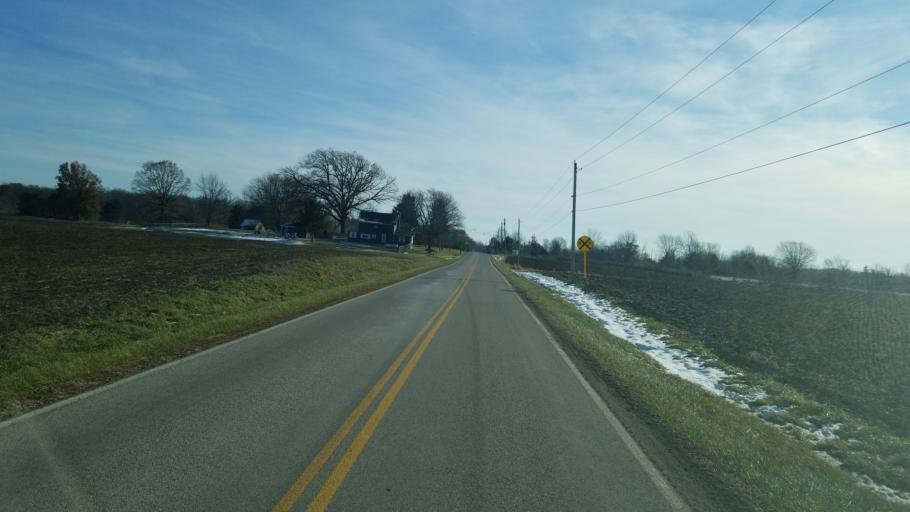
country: US
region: Ohio
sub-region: Lorain County
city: Camden
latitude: 41.1873
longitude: -82.3552
